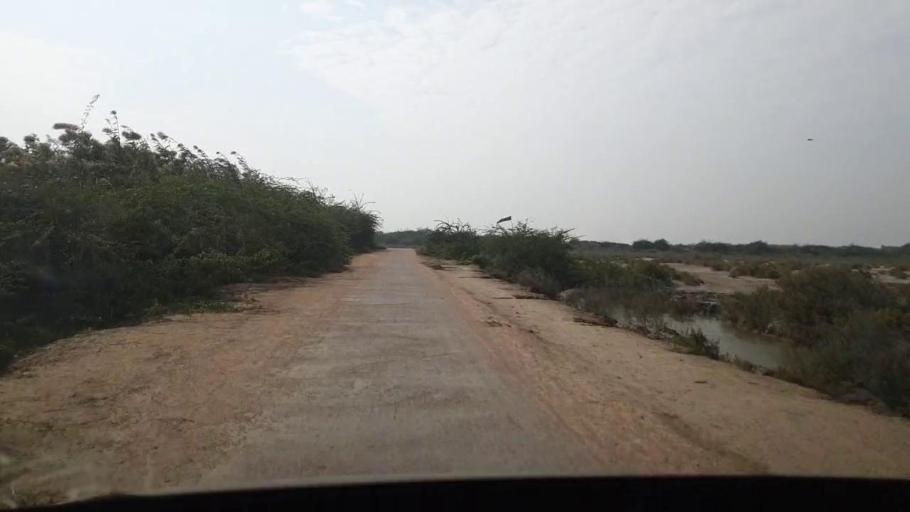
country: PK
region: Sindh
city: Chuhar Jamali
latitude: 24.2405
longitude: 67.9862
